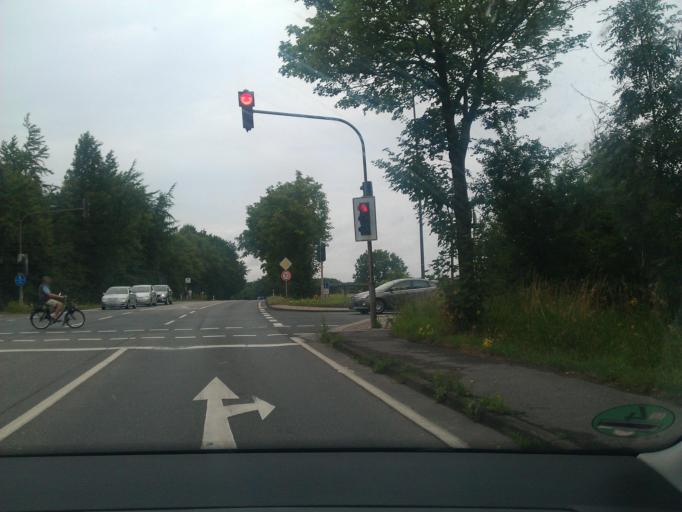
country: BE
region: Wallonia
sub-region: Province de Liege
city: Raeren
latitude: 50.7156
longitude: 6.1321
